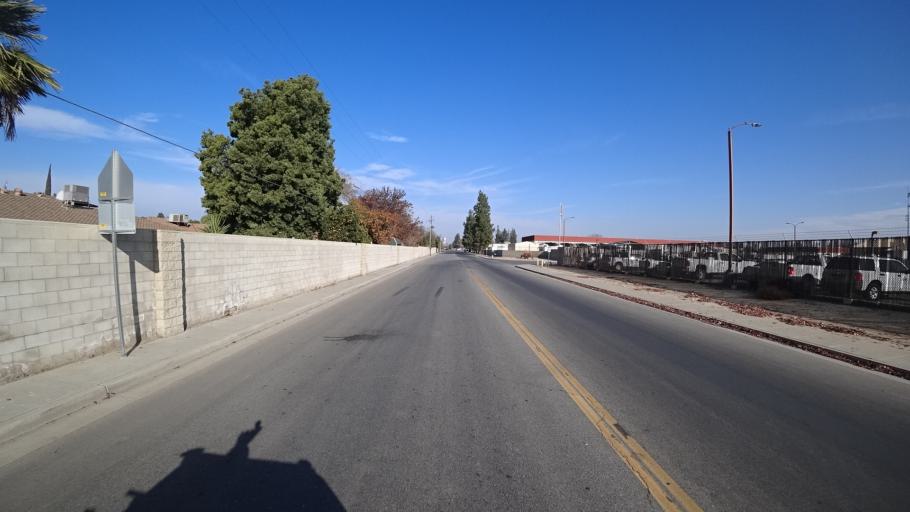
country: US
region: California
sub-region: Kern County
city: Oildale
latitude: 35.4091
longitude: -119.0622
